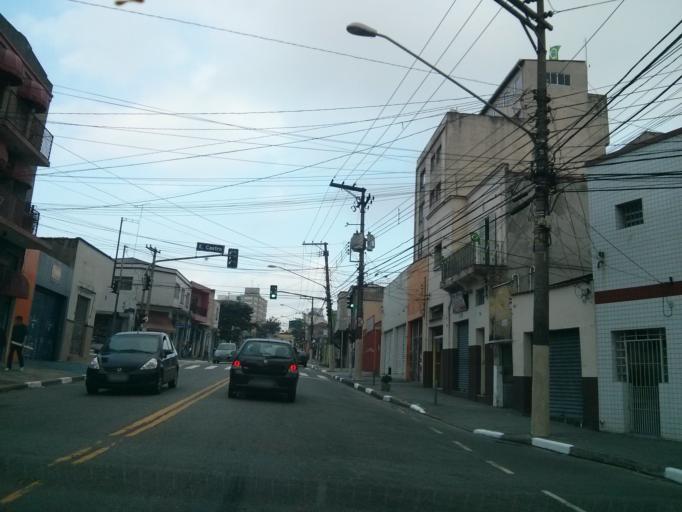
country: BR
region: Sao Paulo
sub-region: Sao Paulo
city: Sao Paulo
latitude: -23.5992
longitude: -46.6162
